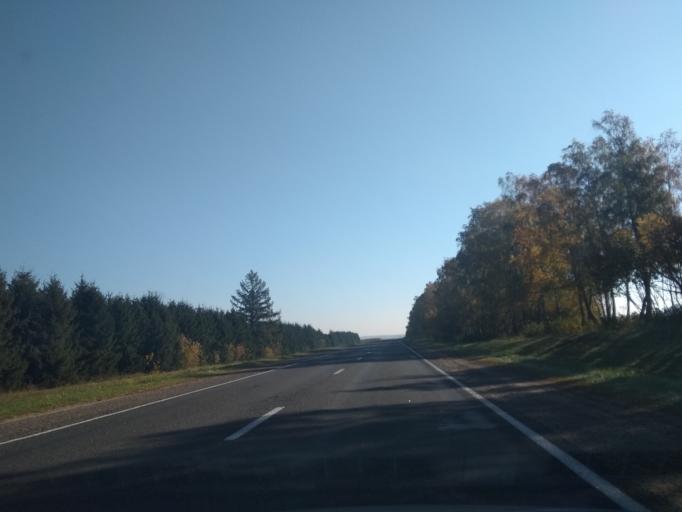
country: BY
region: Grodnenskaya
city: Slonim
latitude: 53.1208
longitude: 25.1049
